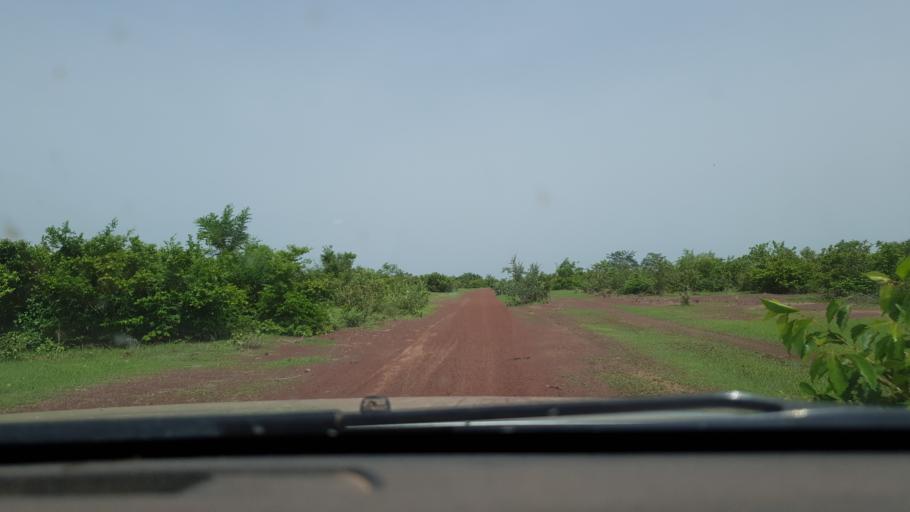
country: ML
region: Koulikoro
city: Koulikoro
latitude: 12.6660
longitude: -7.2310
